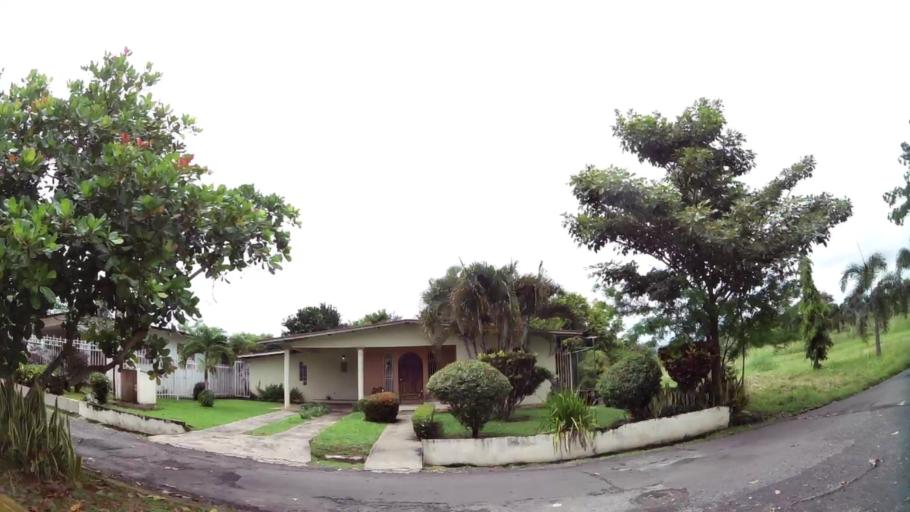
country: PA
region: Chiriqui
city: David
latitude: 8.4207
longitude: -82.4520
